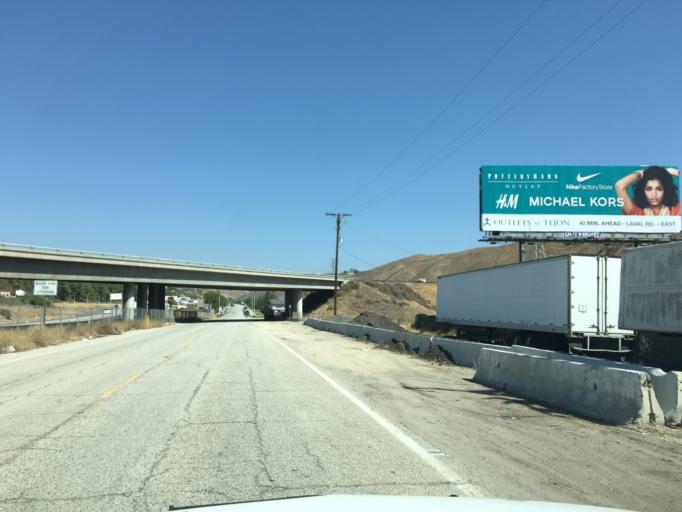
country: US
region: California
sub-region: Los Angeles County
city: Castaic
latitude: 34.5017
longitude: -118.6267
